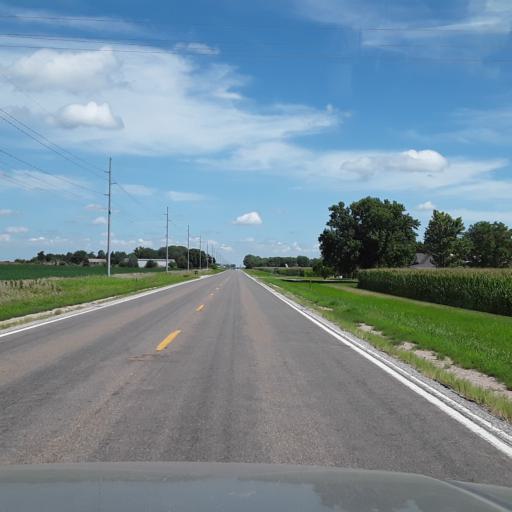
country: US
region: Nebraska
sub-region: York County
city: York
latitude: 40.9085
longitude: -97.4063
